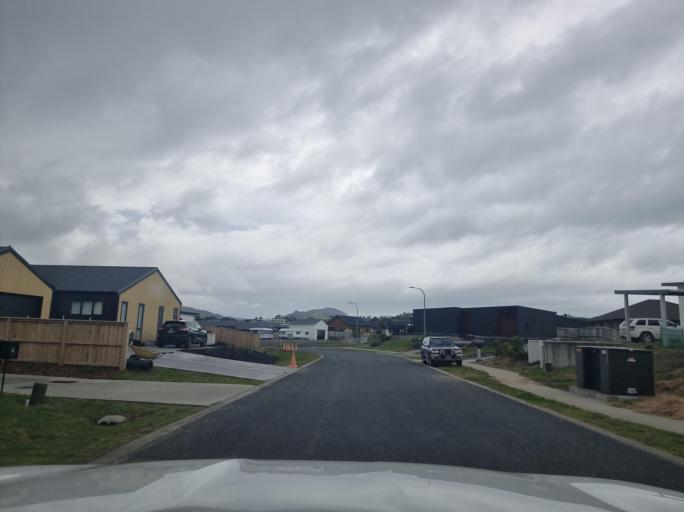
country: NZ
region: Auckland
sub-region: Auckland
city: Wellsford
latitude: -36.0912
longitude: 174.5771
